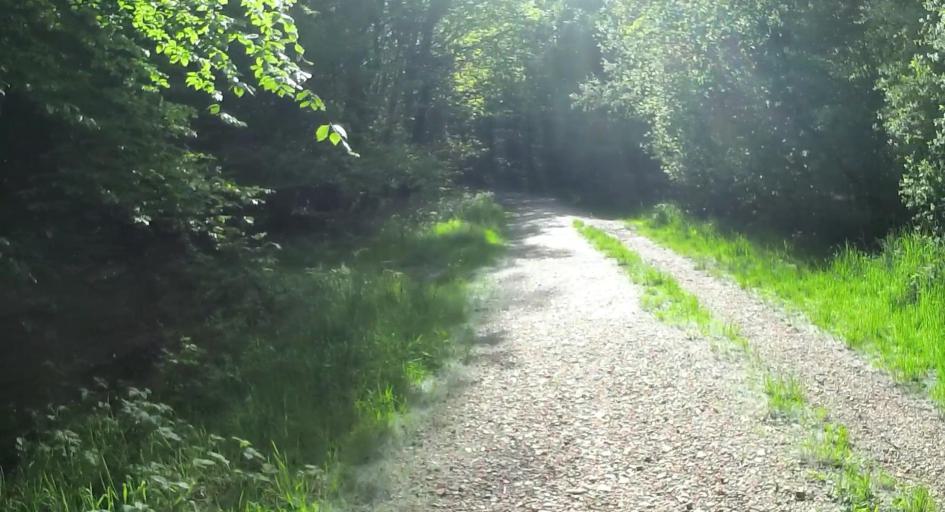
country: GB
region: England
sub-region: Hampshire
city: Lindford
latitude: 51.1694
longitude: -0.8317
